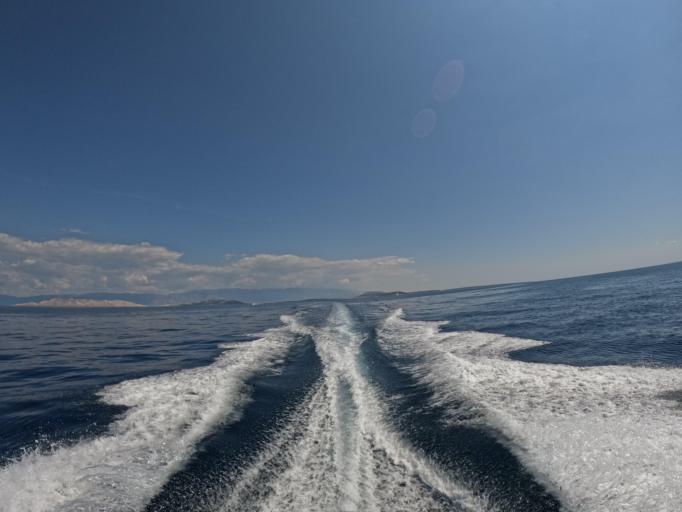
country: HR
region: Primorsko-Goranska
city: Punat
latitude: 44.8972
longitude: 14.6184
